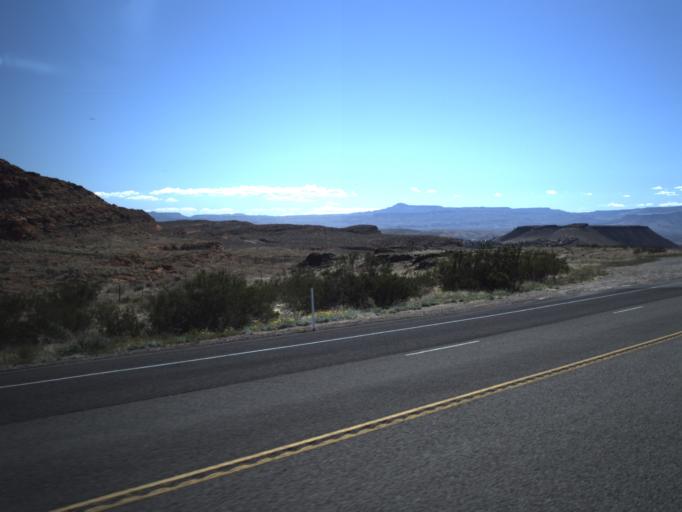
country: US
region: Utah
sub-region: Washington County
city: Santa Clara
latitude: 37.1512
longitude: -113.6074
